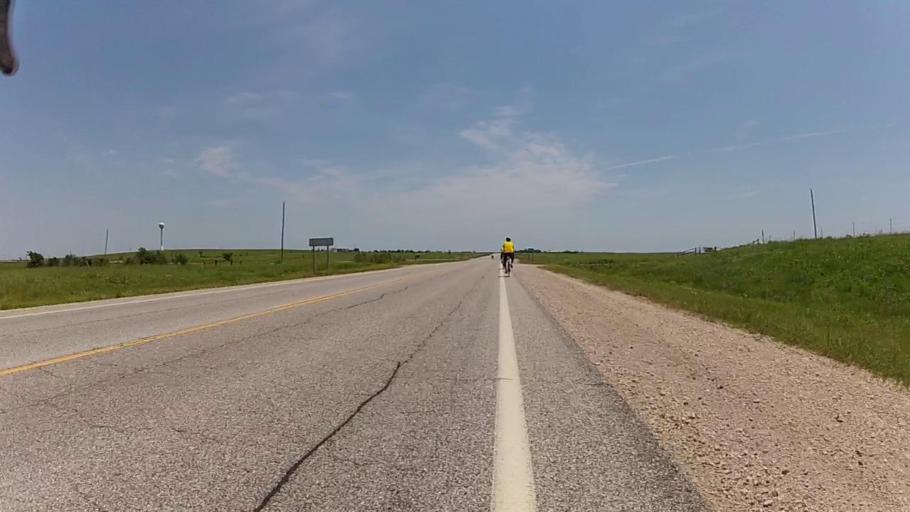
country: US
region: Kansas
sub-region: Chautauqua County
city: Sedan
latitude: 37.1082
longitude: -96.2504
